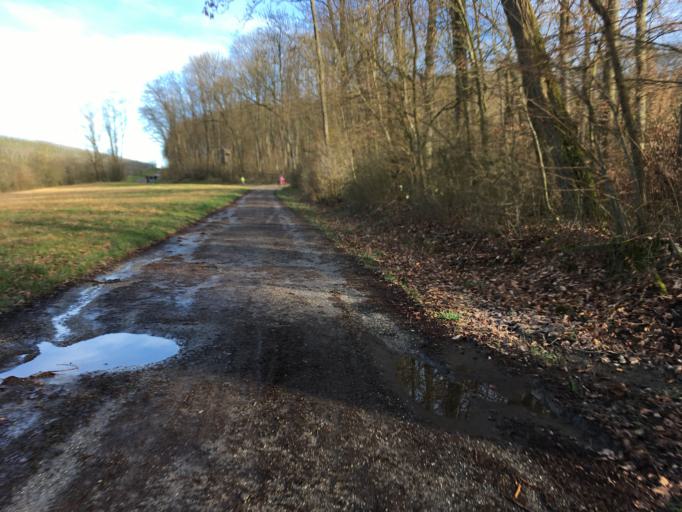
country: DE
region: Baden-Wuerttemberg
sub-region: Regierungsbezirk Stuttgart
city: Lehrensteinsfeld
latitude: 49.1251
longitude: 9.3414
